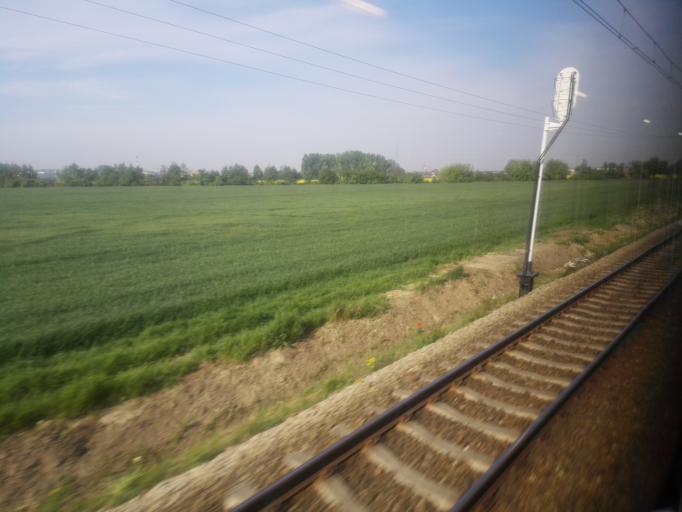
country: PL
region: Greater Poland Voivodeship
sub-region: Powiat wrzesinski
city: Wrzesnia
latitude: 52.3356
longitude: 17.6079
